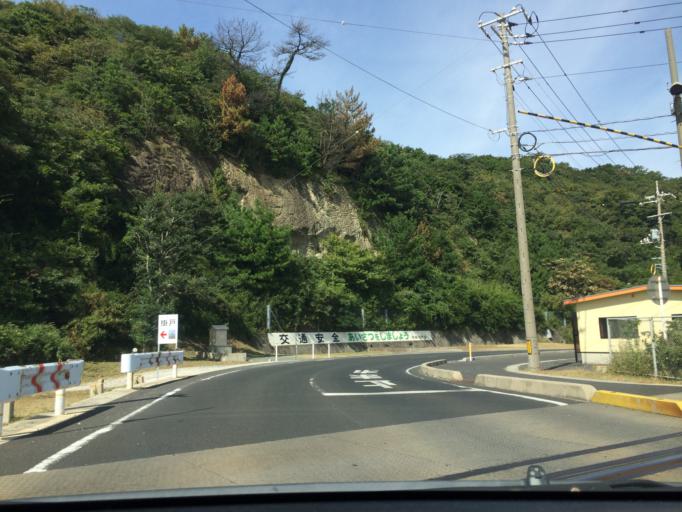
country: JP
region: Shimane
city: Odacho-oda
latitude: 35.2388
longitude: 132.5155
